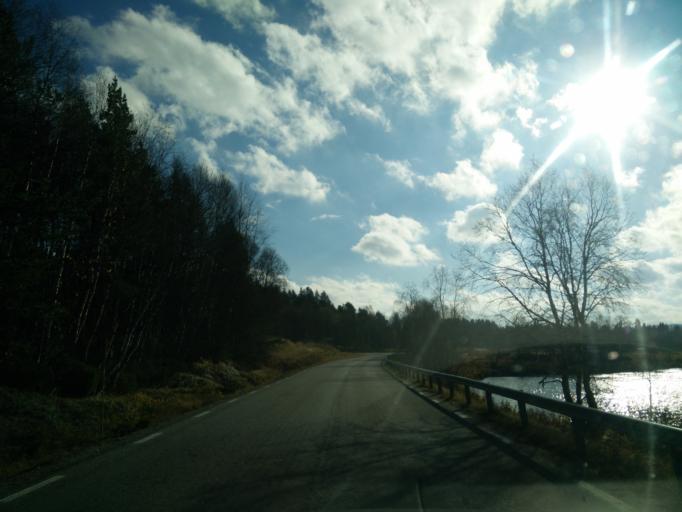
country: SE
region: Jaemtland
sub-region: Are Kommun
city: Are
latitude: 62.5451
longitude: 12.6123
